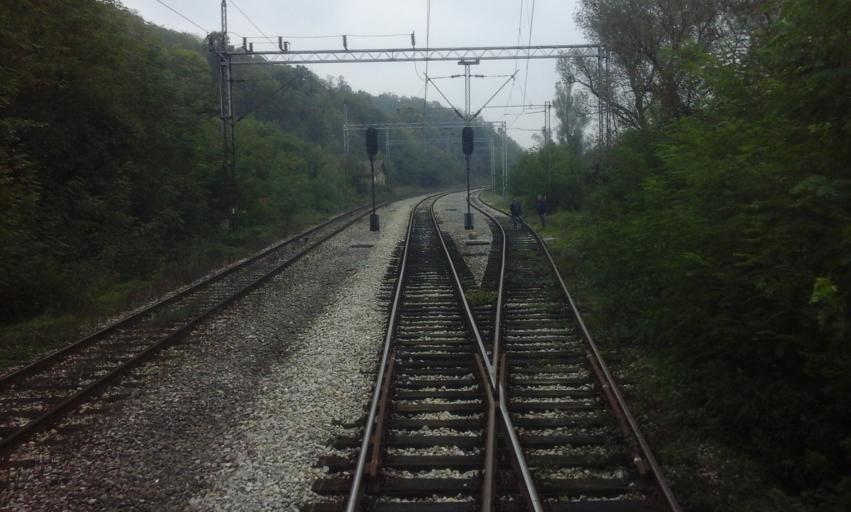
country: RS
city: Rusanj
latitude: 44.6453
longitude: 20.5331
